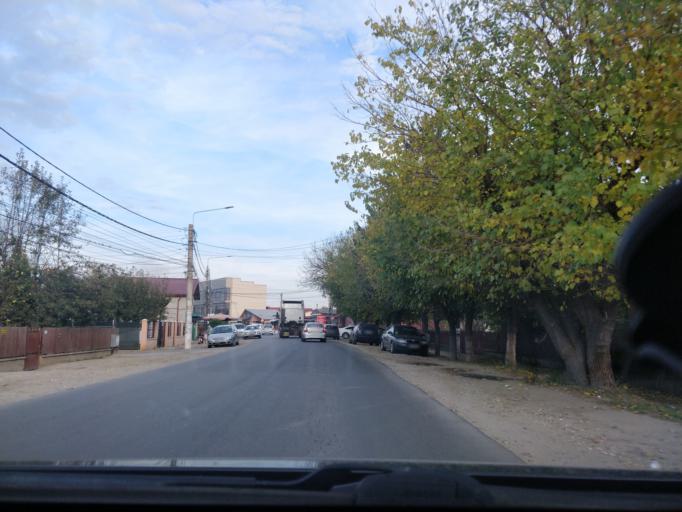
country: RO
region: Giurgiu
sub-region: Comuna Bolintin Vale
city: Bolintin Vale
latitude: 44.4472
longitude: 25.7532
